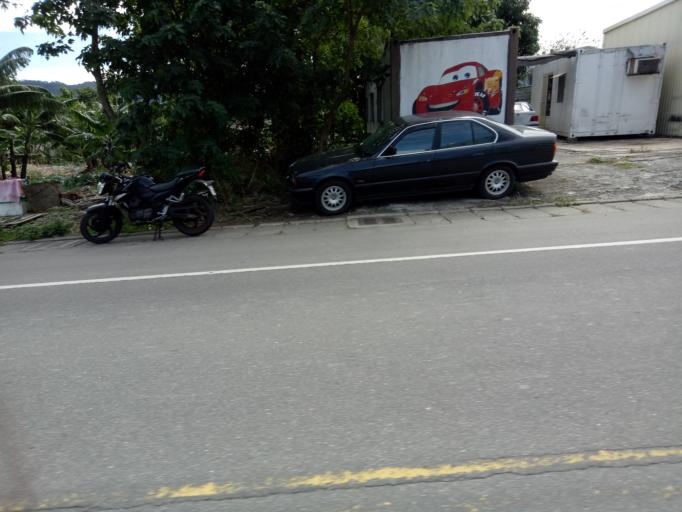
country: TW
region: Taiwan
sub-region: Taoyuan
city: Taoyuan
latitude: 24.9345
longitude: 121.3217
